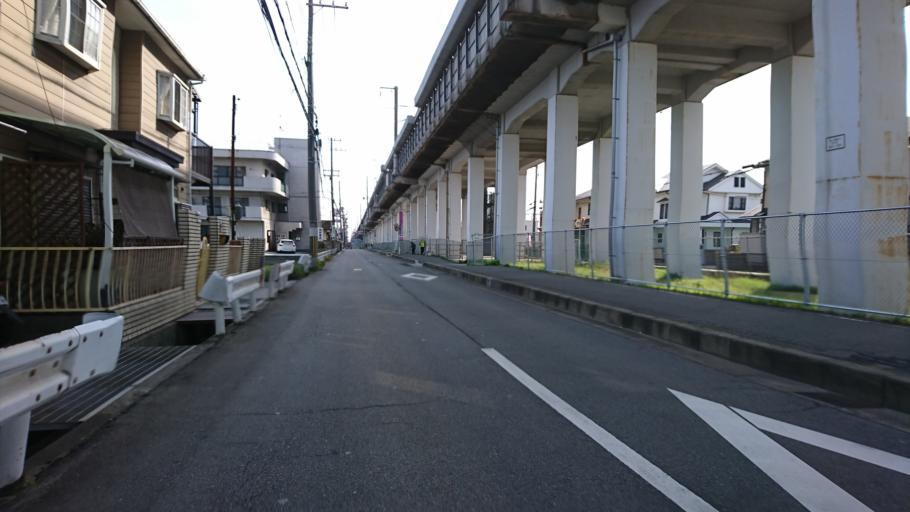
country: JP
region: Hyogo
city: Kakogawacho-honmachi
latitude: 34.7430
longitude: 134.8329
